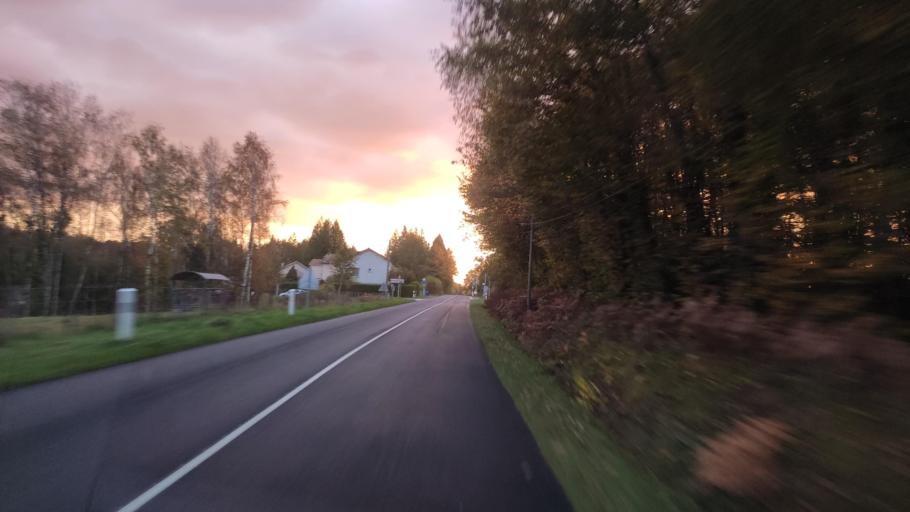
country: FR
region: Limousin
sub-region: Departement de la Haute-Vienne
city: Rilhac-Rancon
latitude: 45.9142
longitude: 1.3318
